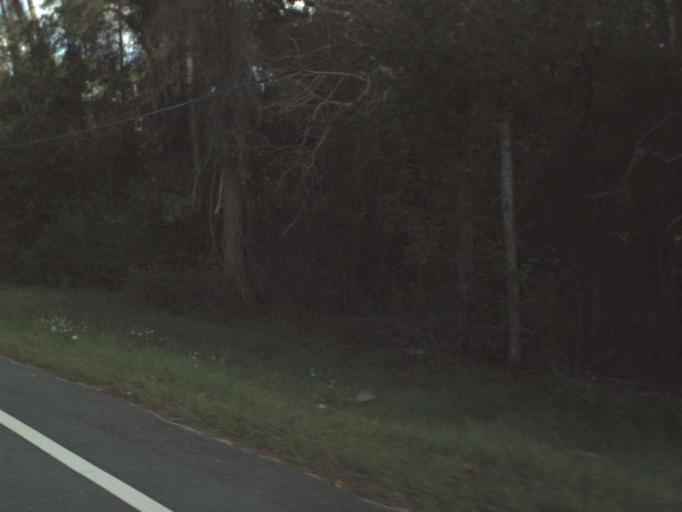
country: US
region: Florida
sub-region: Washington County
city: Chipley
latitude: 30.7471
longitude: -85.5932
